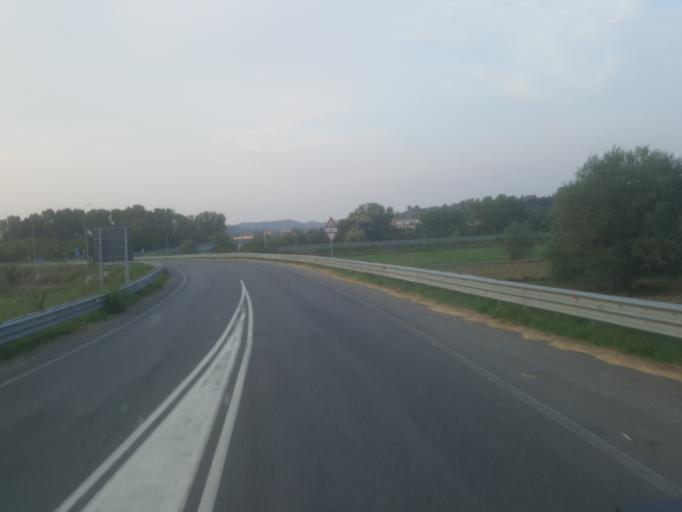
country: IT
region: Tuscany
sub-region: Province of Florence
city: Certaldo
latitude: 43.5318
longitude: 11.0401
